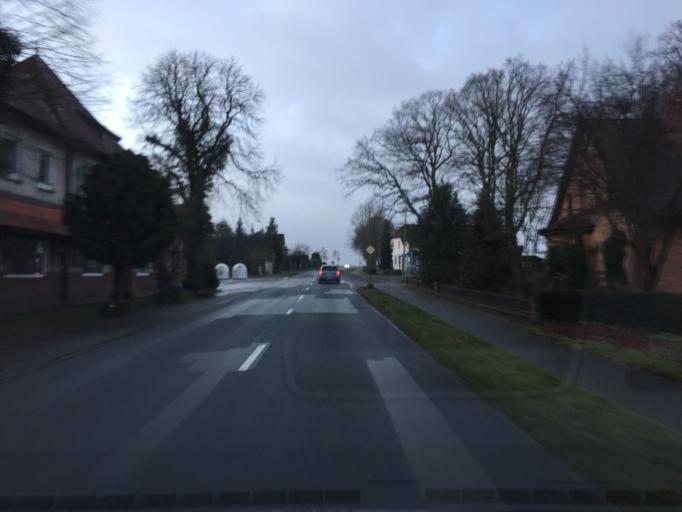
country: DE
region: Lower Saxony
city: Pennigsehl
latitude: 52.6371
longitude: 9.0239
